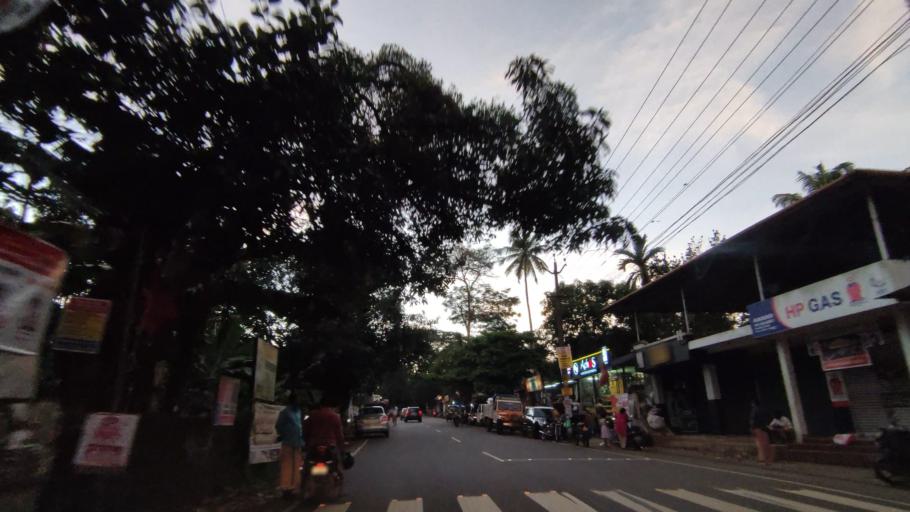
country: IN
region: Kerala
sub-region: Kottayam
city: Vaikam
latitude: 9.6958
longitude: 76.4829
